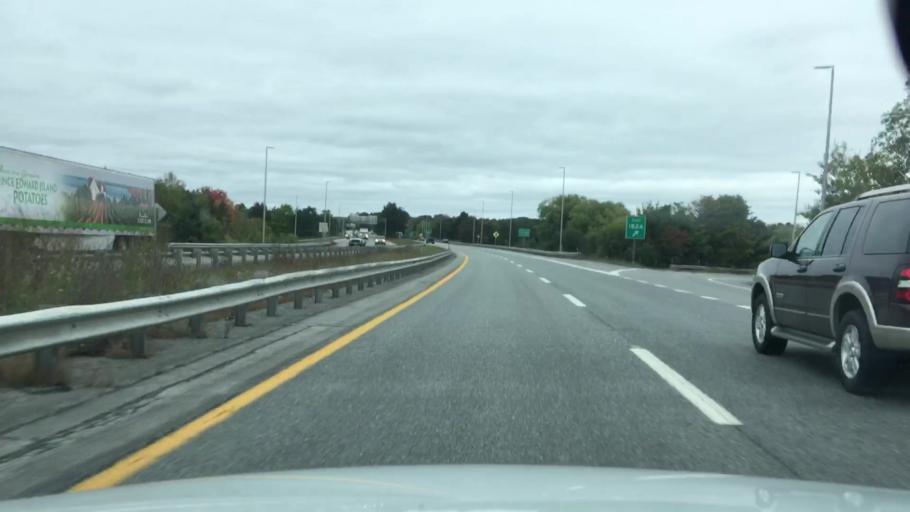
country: US
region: Maine
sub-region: Penobscot County
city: Bangor
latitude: 44.7842
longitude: -68.8105
